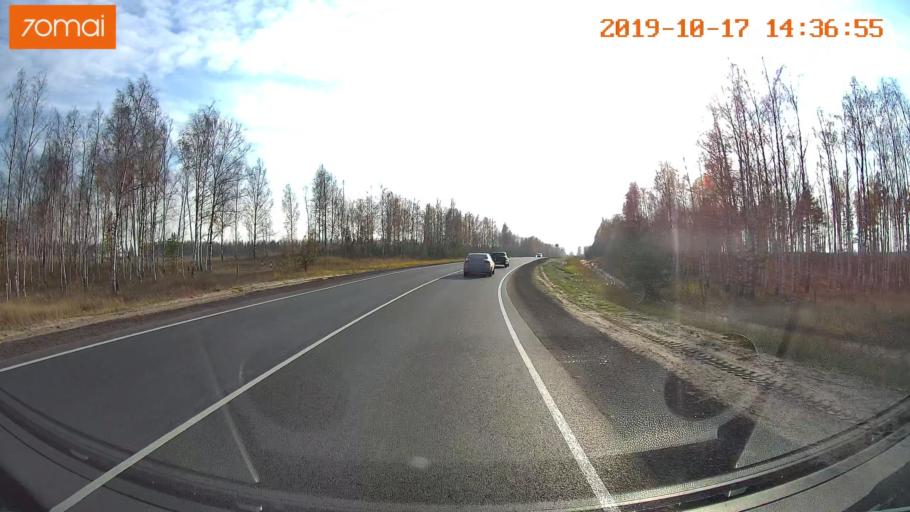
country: RU
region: Rjazan
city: Solotcha
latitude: 54.8851
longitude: 40.0007
